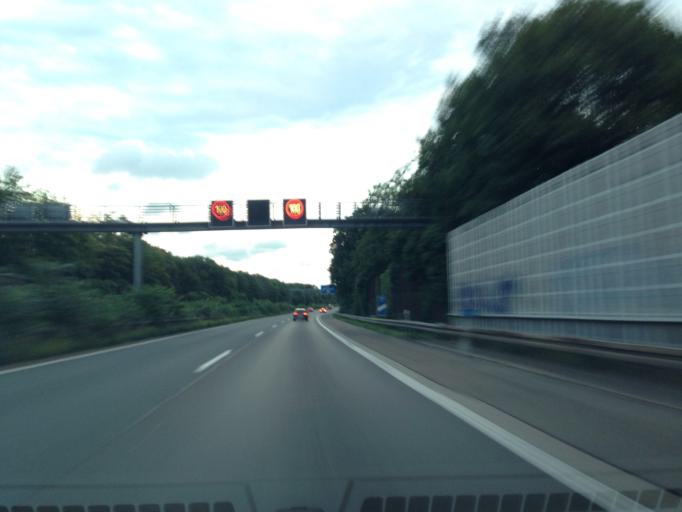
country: DE
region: North Rhine-Westphalia
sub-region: Regierungsbezirk Dusseldorf
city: Krefeld
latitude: 51.3376
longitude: 6.6252
